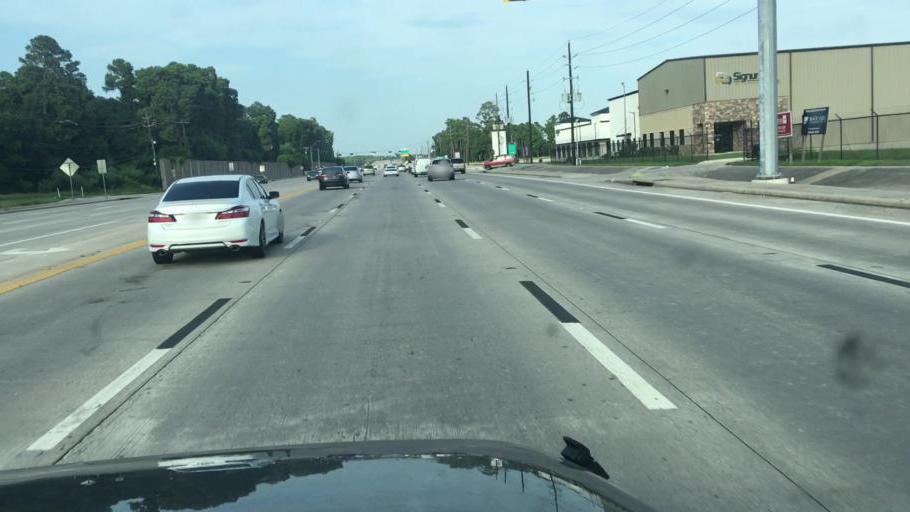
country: US
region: Texas
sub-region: Harris County
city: Spring
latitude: 30.0241
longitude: -95.4174
